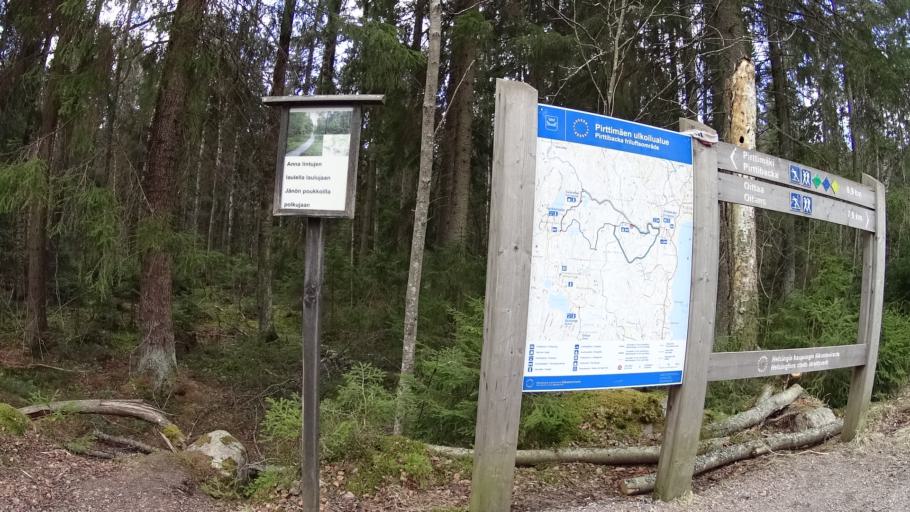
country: FI
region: Uusimaa
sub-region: Helsinki
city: Espoo
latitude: 60.2697
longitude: 24.6379
